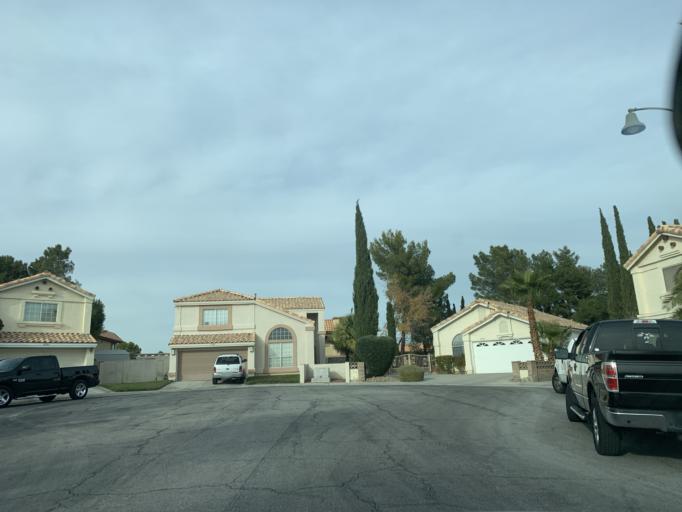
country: US
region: Nevada
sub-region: Clark County
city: Summerlin South
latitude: 36.1422
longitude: -115.3032
